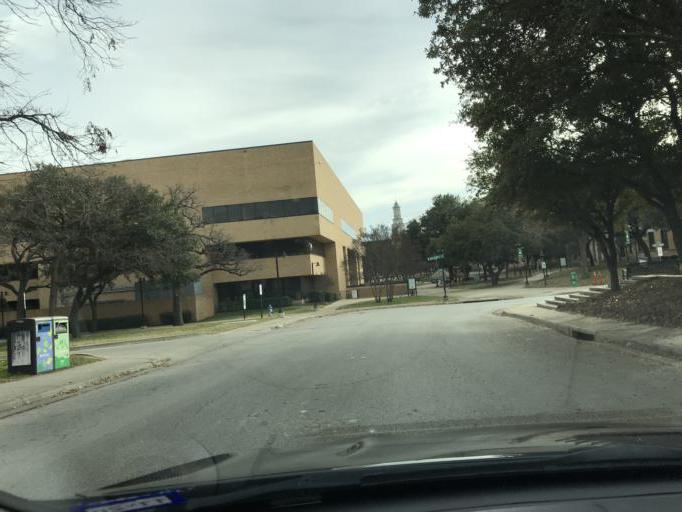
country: US
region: Texas
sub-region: Denton County
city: Denton
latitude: 33.2140
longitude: -97.1484
